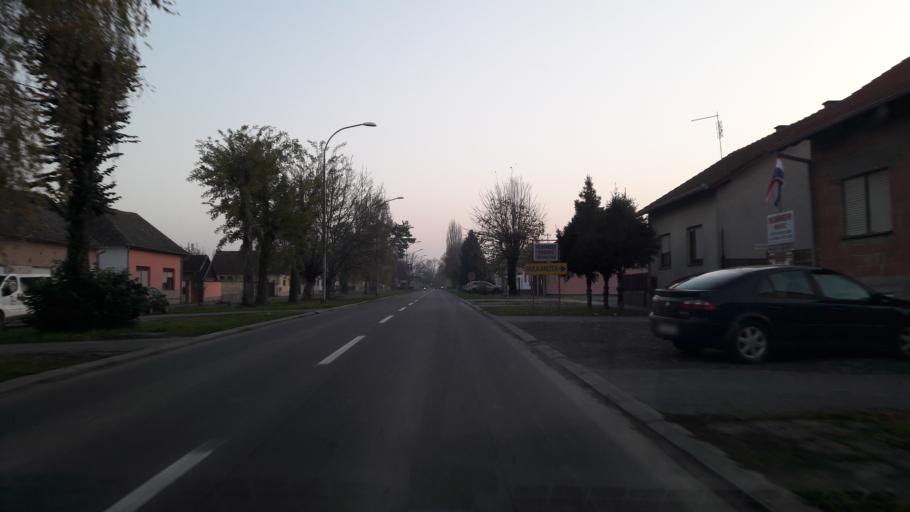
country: HR
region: Vukovarsko-Srijemska
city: Vukovar
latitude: 45.3425
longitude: 19.0026
